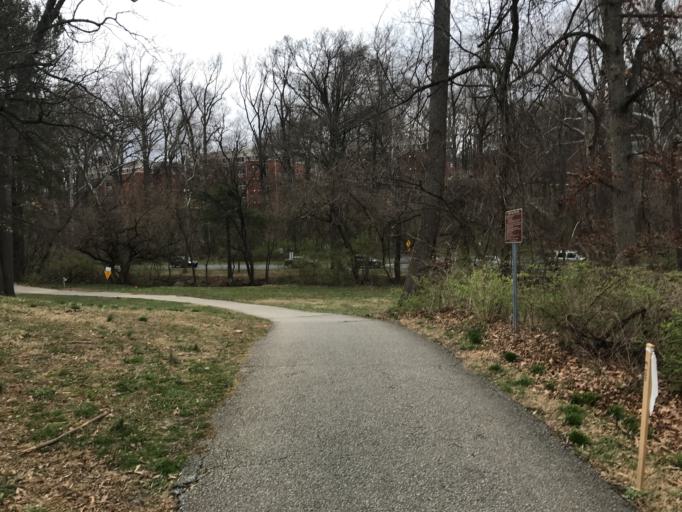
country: US
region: Maryland
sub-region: Montgomery County
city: Silver Spring
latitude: 39.0002
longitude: -77.0114
